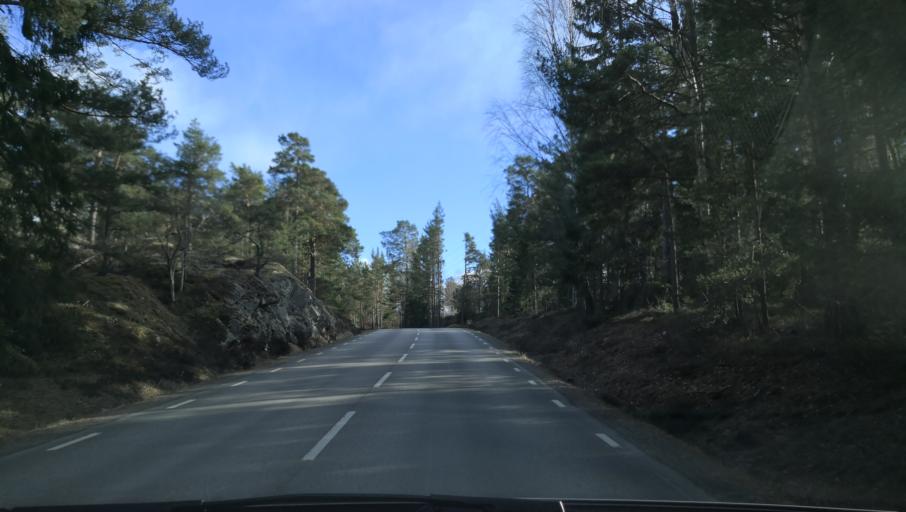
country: SE
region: Stockholm
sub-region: Varmdo Kommun
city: Hemmesta
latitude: 59.2273
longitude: 18.5254
